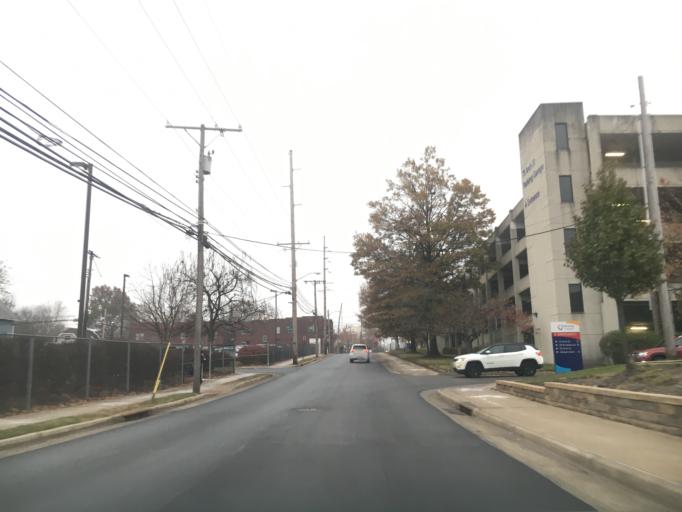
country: US
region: Ohio
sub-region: Summit County
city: Akron
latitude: 41.0812
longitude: -81.4983
